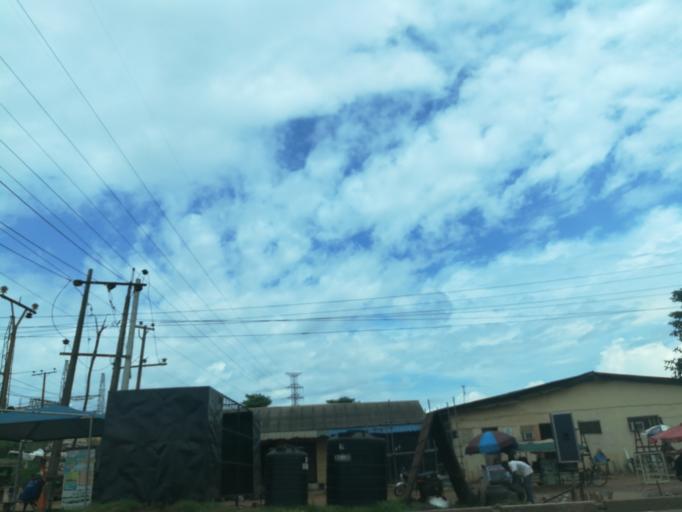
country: NG
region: Lagos
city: Ikorodu
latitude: 6.6243
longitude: 3.5051
